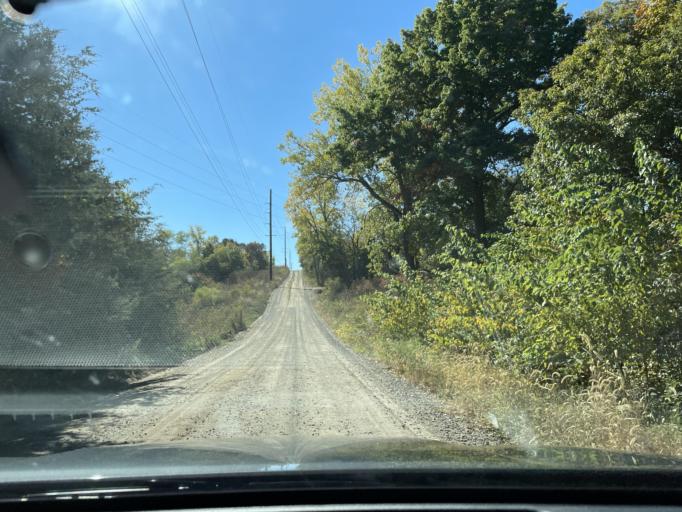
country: US
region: Missouri
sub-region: Andrew County
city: Savannah
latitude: 39.9272
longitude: -94.8612
